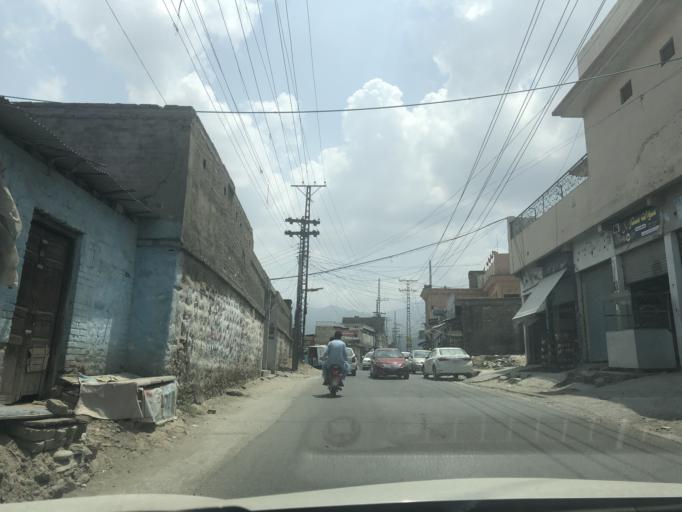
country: PK
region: Khyber Pakhtunkhwa
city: Mingora
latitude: 34.7714
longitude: 72.3496
